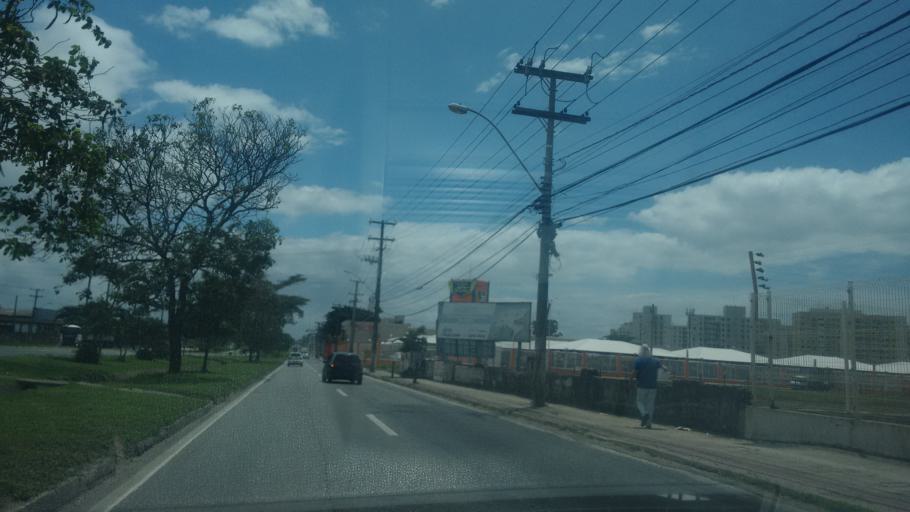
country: BR
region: Espirito Santo
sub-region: Serra
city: Serra
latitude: -20.2029
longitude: -40.2689
